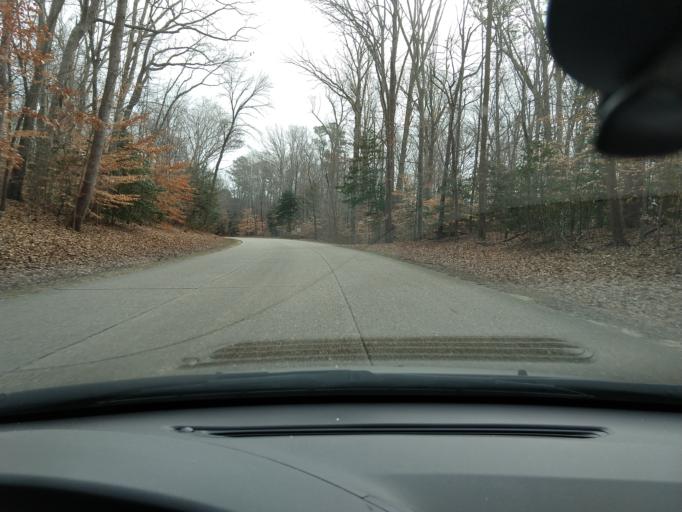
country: US
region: Virginia
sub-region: City of Williamsburg
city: Williamsburg
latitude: 37.2778
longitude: -76.6659
